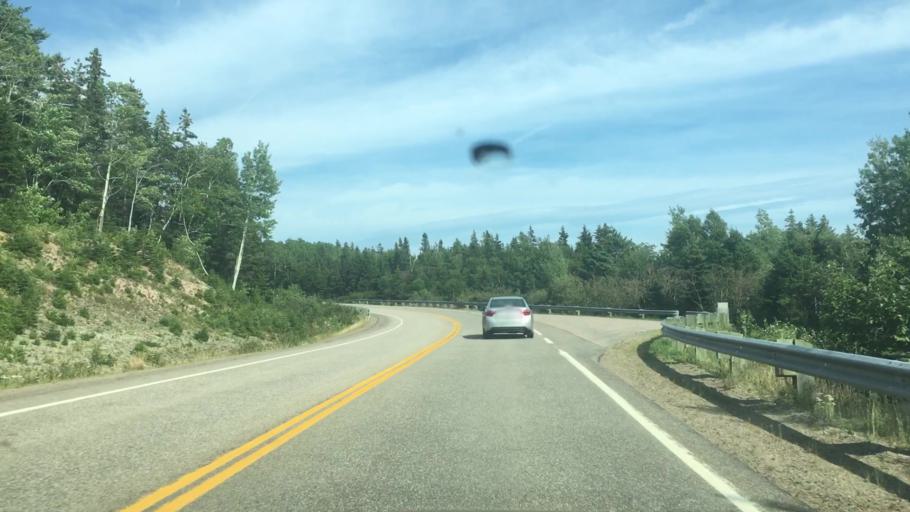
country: CA
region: Nova Scotia
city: Sydney Mines
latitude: 46.7138
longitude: -60.3563
